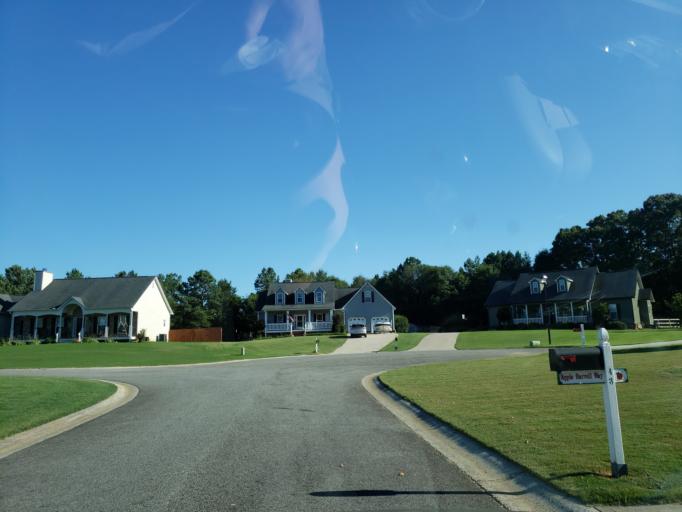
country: US
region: Georgia
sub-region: Bartow County
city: Euharlee
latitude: 34.1065
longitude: -84.9996
